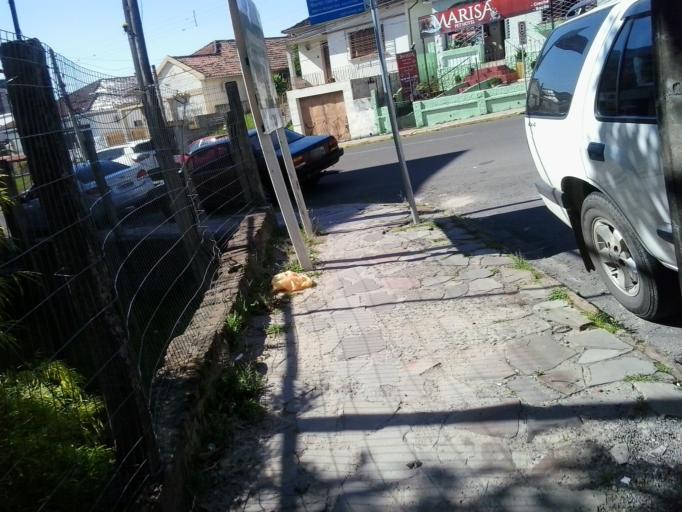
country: BR
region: Rio Grande do Sul
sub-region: Santa Maria
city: Santa Maria
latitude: -29.6876
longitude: -53.7979
